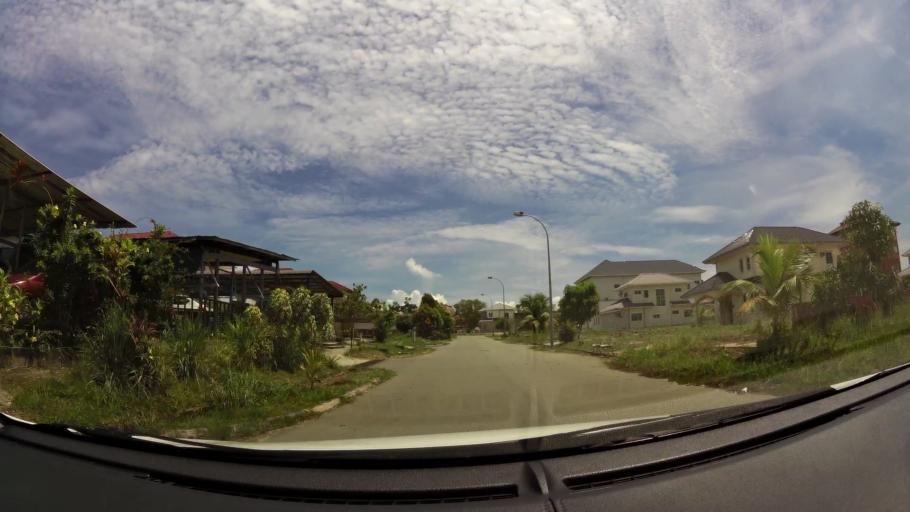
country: BN
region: Brunei and Muara
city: Bandar Seri Begawan
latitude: 4.9668
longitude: 114.9017
